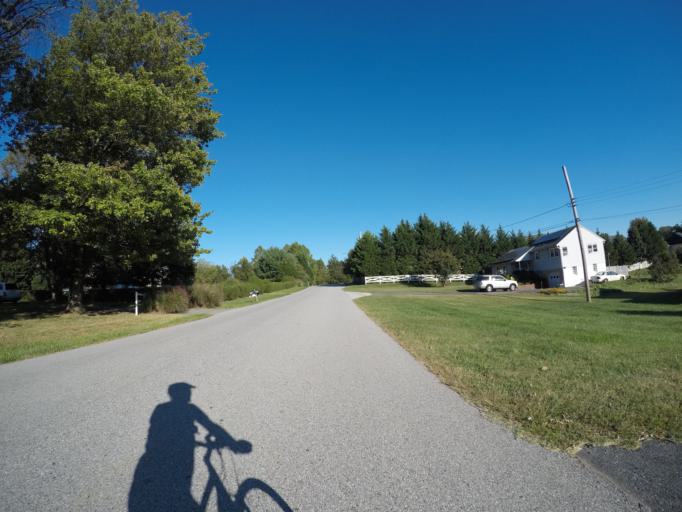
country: US
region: Maryland
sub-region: Howard County
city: Ellicott City
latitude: 39.2957
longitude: -76.8059
